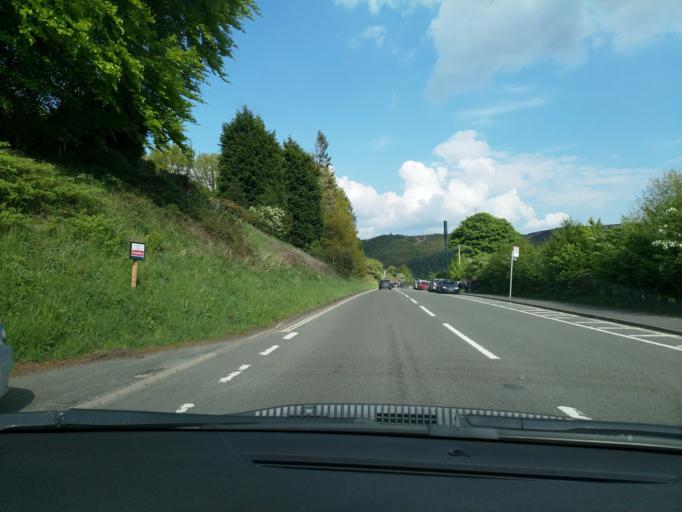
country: GB
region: England
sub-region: Derbyshire
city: Hope Valley
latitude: 53.3746
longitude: -1.7080
